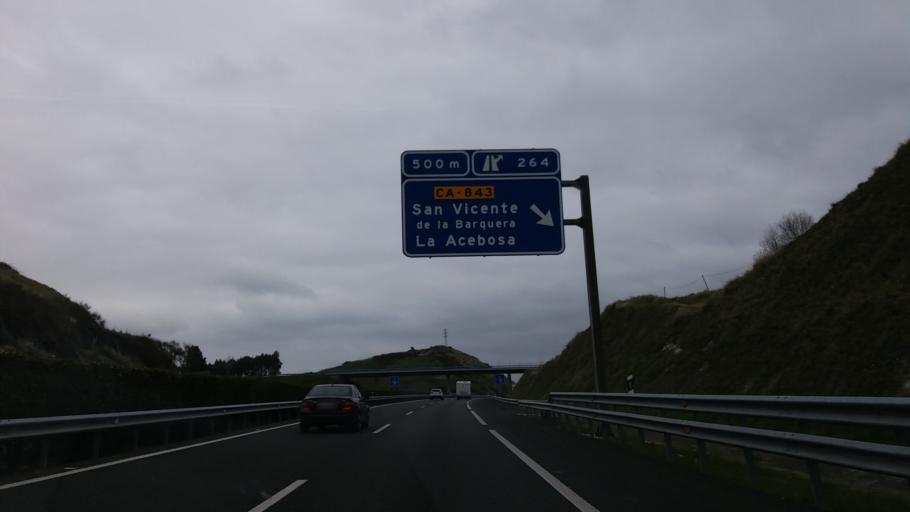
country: ES
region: Cantabria
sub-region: Provincia de Cantabria
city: San Vicente de la Barquera
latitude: 43.3710
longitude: -4.4122
